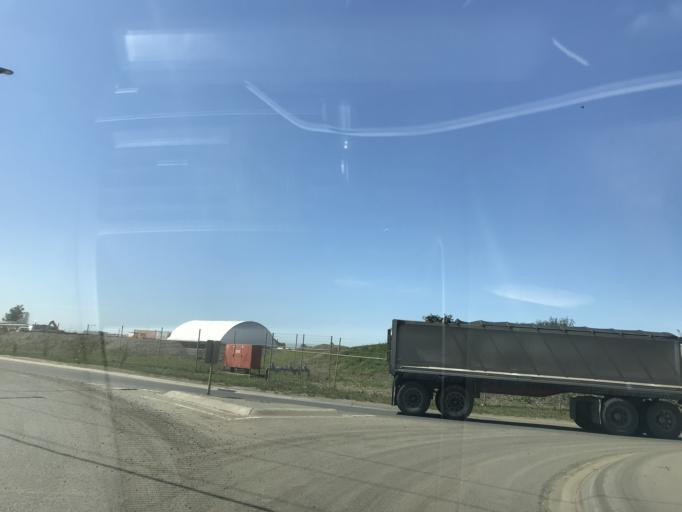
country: AU
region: Victoria
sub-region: Wyndham
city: Truganina
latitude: -37.8304
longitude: 144.7698
